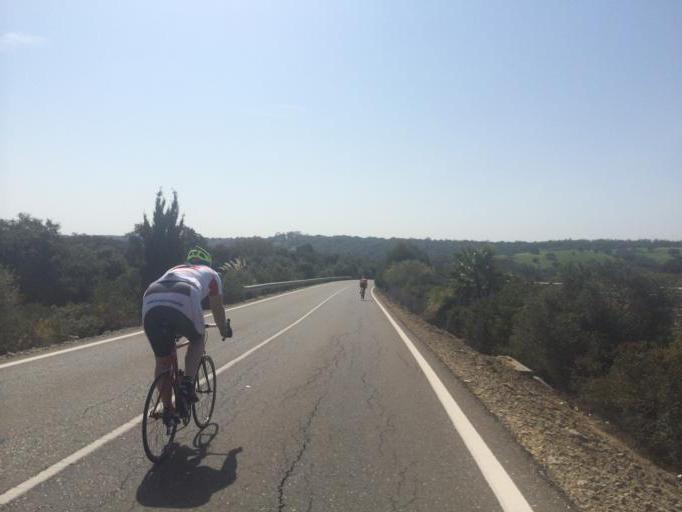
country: ES
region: Andalusia
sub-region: Provincia de Cadiz
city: San Roque
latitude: 36.2693
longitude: -5.3166
